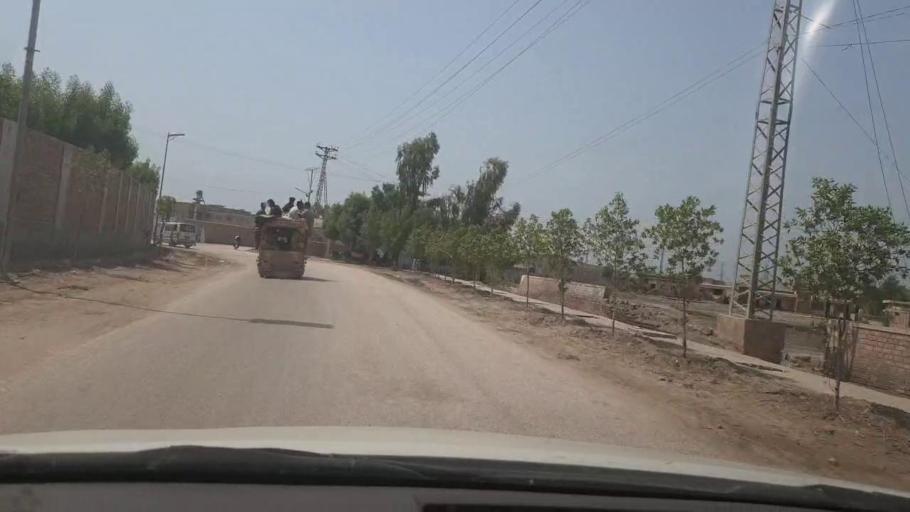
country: PK
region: Sindh
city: Garhi Yasin
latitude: 27.9103
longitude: 68.5120
